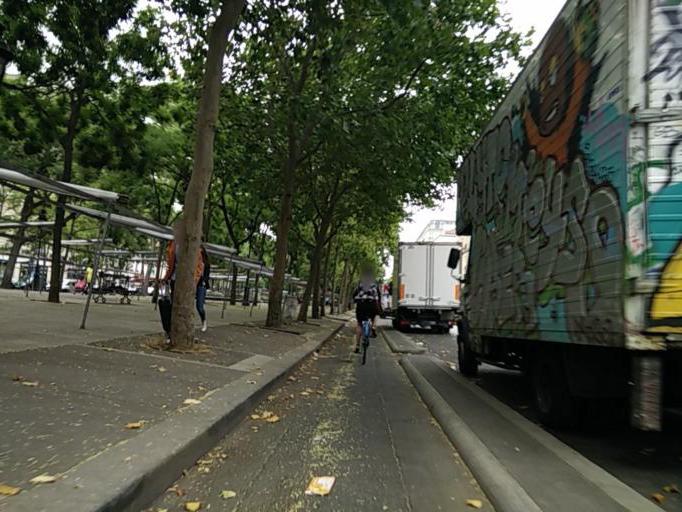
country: FR
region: Ile-de-France
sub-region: Paris
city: Paris
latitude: 48.8653
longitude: 2.3699
